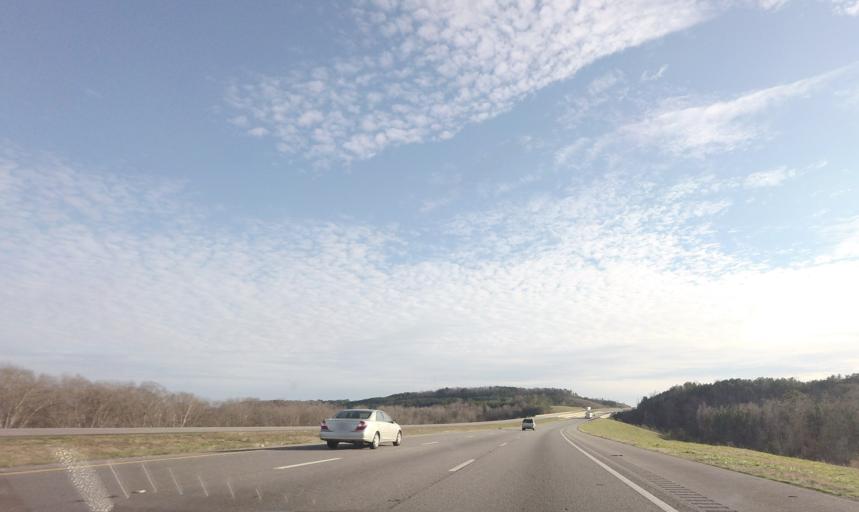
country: US
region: Alabama
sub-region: Walker County
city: Cordova
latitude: 33.7802
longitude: -87.2104
